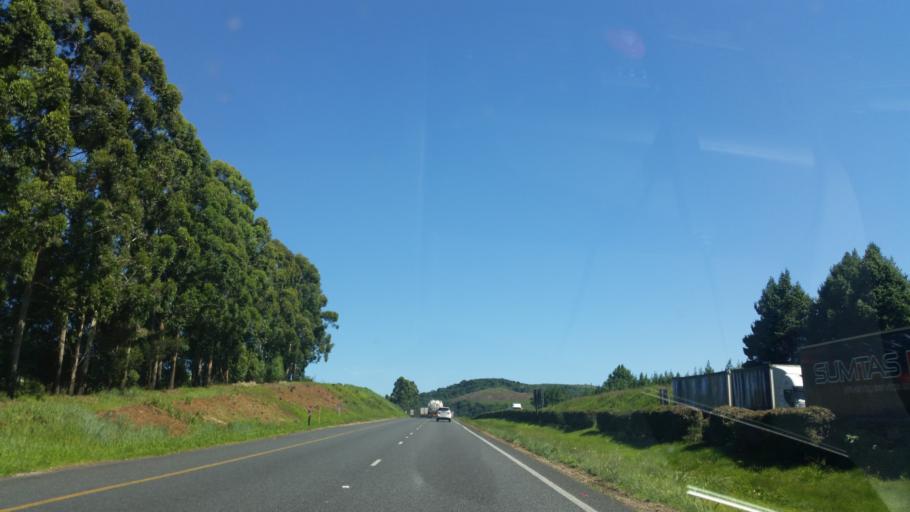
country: ZA
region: KwaZulu-Natal
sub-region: uMgungundlovu District Municipality
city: Mooirivier
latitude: -29.3534
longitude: 30.0883
